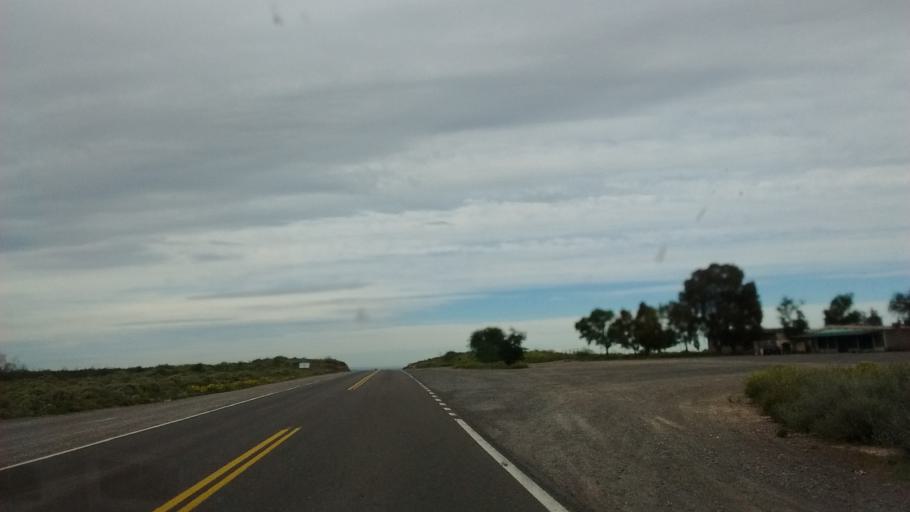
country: AR
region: Rio Negro
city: Contraalmirante Cordero
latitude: -38.3978
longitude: -68.0291
